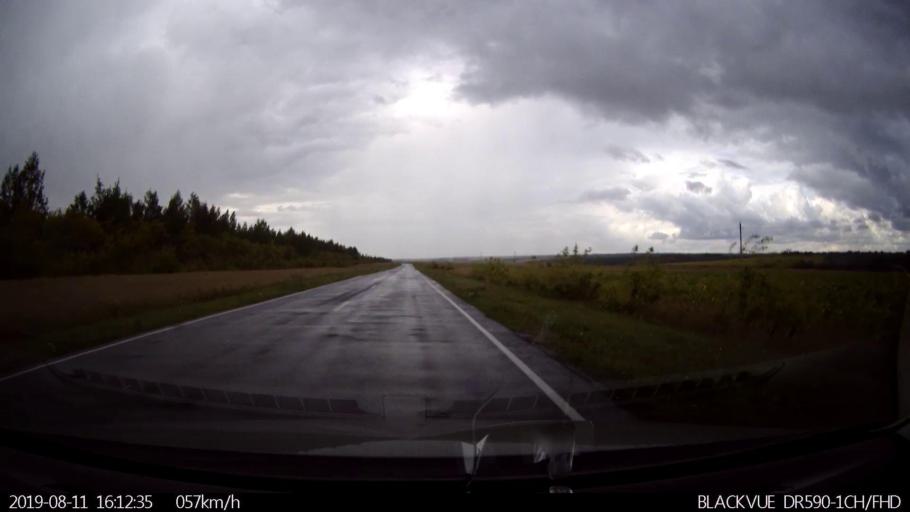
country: RU
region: Ulyanovsk
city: Ignatovka
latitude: 54.0127
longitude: 47.6400
